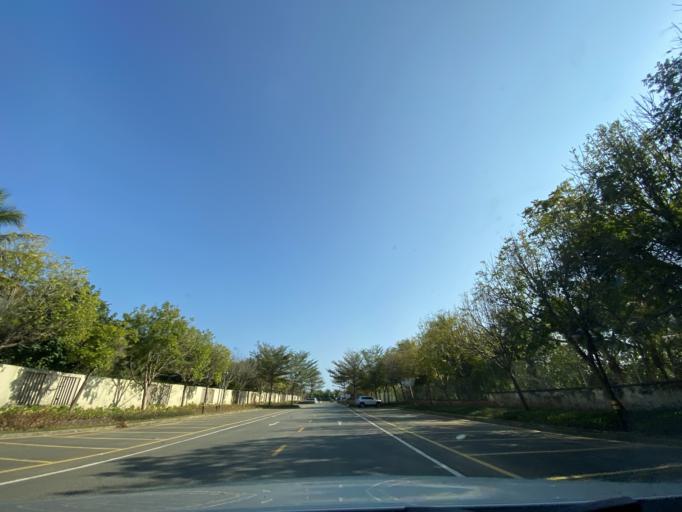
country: CN
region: Hainan
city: Yingzhou
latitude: 18.4154
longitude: 109.8971
